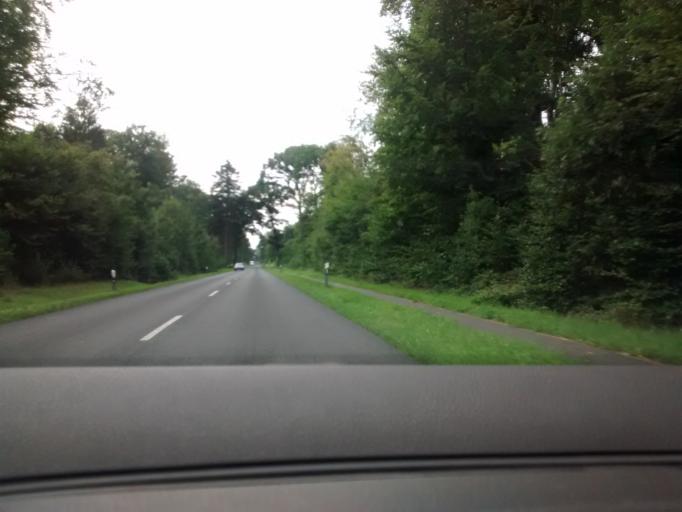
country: DE
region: Lower Saxony
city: Brietlingen
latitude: 53.3188
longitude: 10.4779
